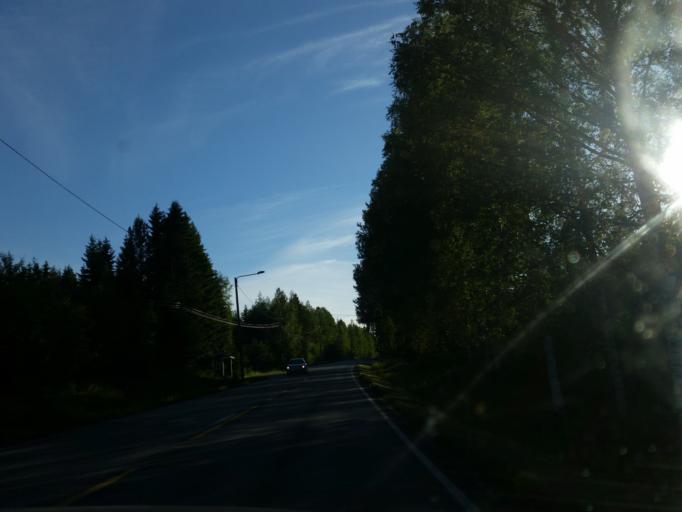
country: FI
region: Northern Savo
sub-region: Kuopio
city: Kuopio
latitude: 62.8444
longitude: 27.4256
